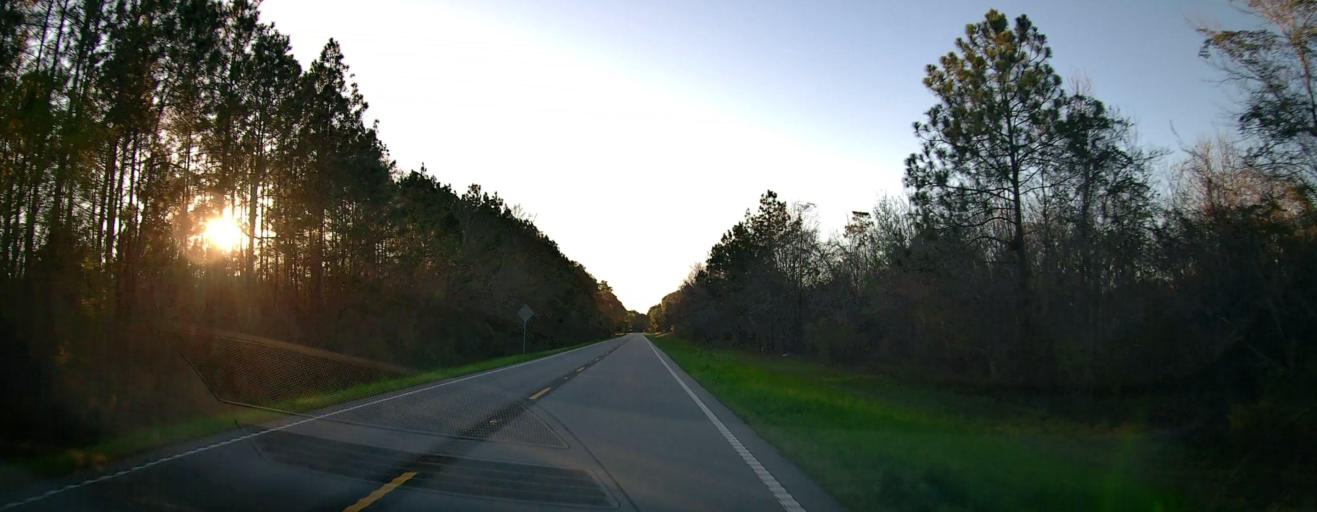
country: US
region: Georgia
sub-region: Wilcox County
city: Rochelle
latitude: 31.9490
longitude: -83.5649
